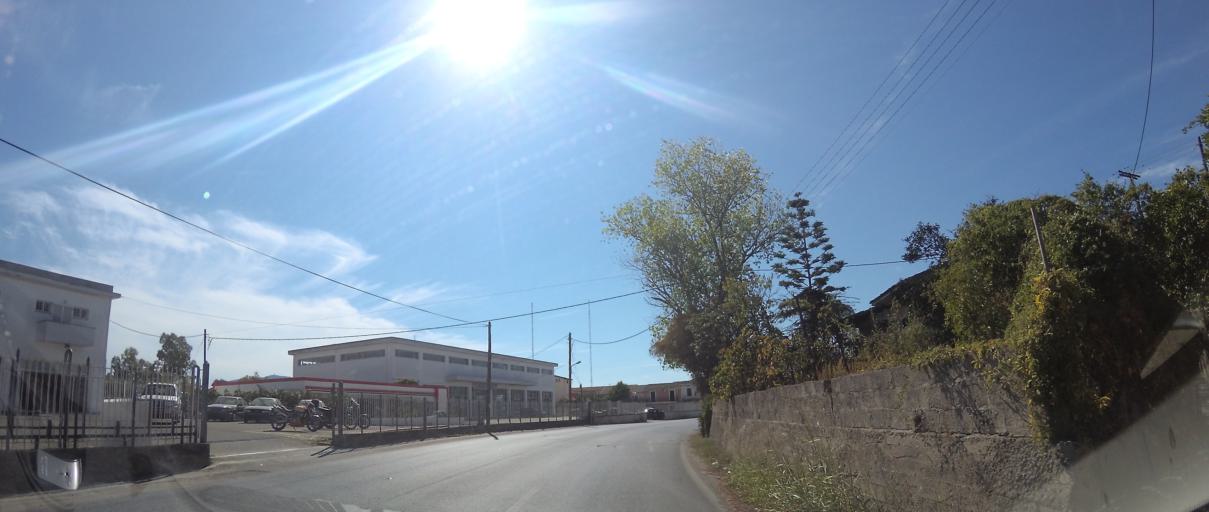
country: GR
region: Ionian Islands
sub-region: Nomos Kerkyras
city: Alepou
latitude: 39.6113
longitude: 19.9068
